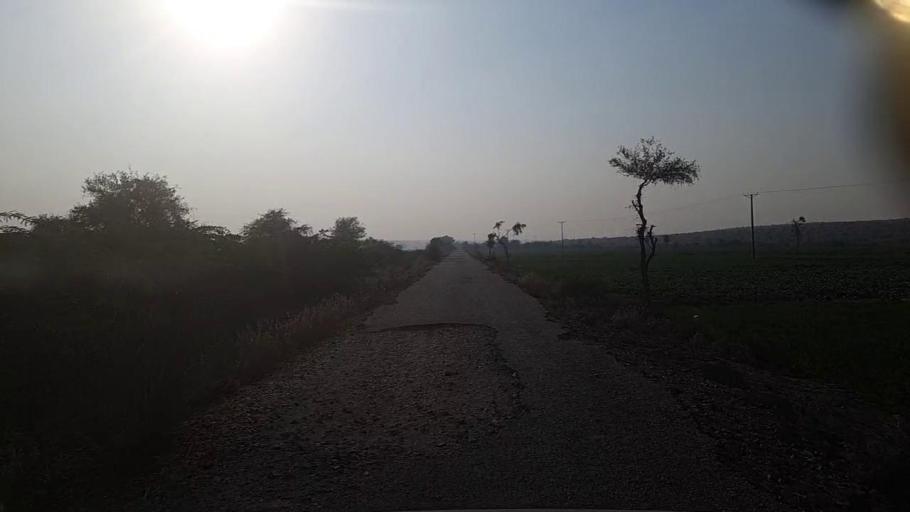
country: PK
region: Sindh
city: Pad Idan
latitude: 26.7158
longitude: 68.4853
